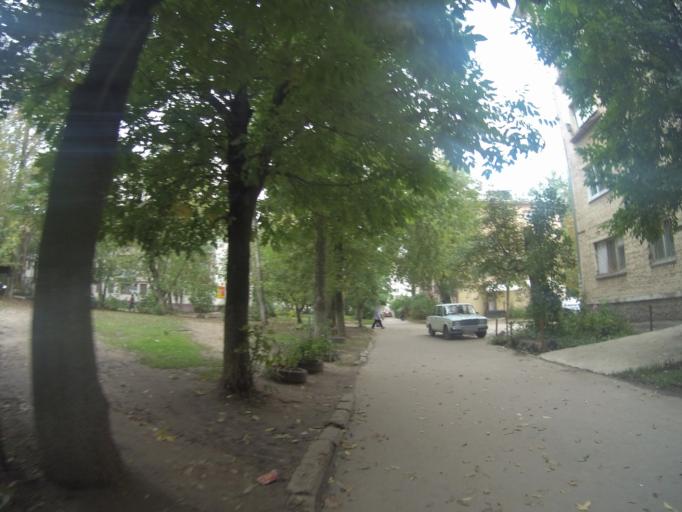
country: RU
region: Vladimir
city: Vladimir
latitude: 56.1165
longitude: 40.3481
